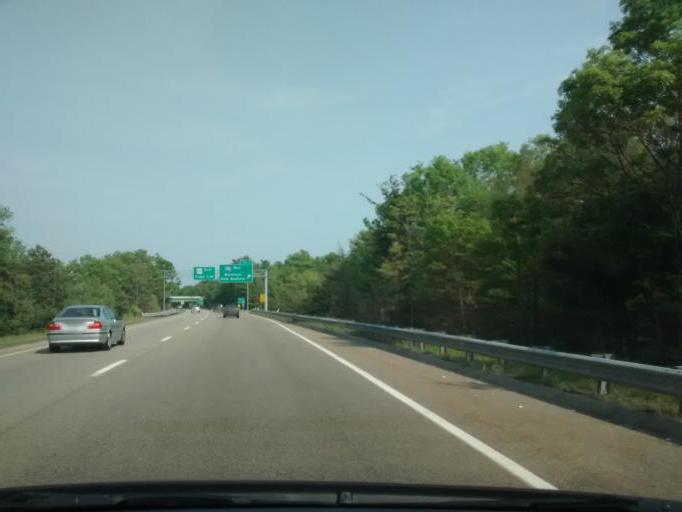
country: US
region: Massachusetts
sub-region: Plymouth County
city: Wareham Center
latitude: 41.7854
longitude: -70.7366
